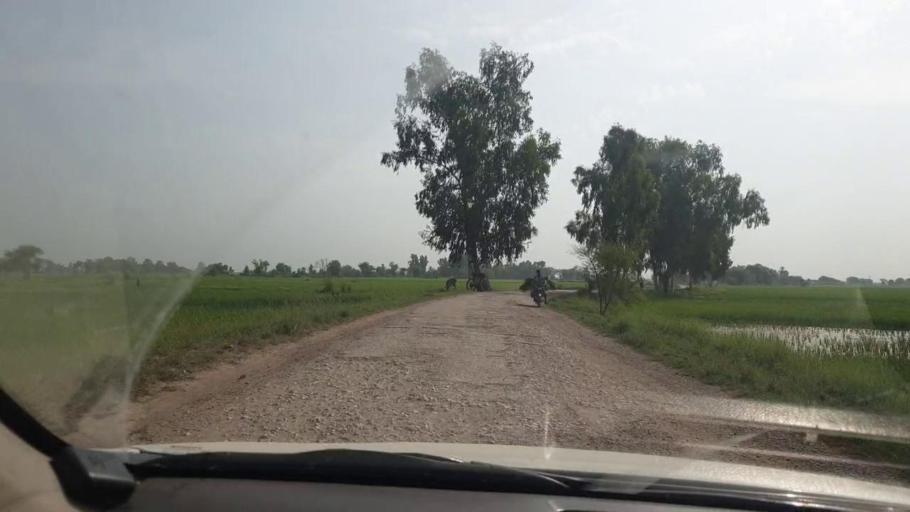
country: PK
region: Sindh
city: Lakhi
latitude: 27.8282
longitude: 68.7375
